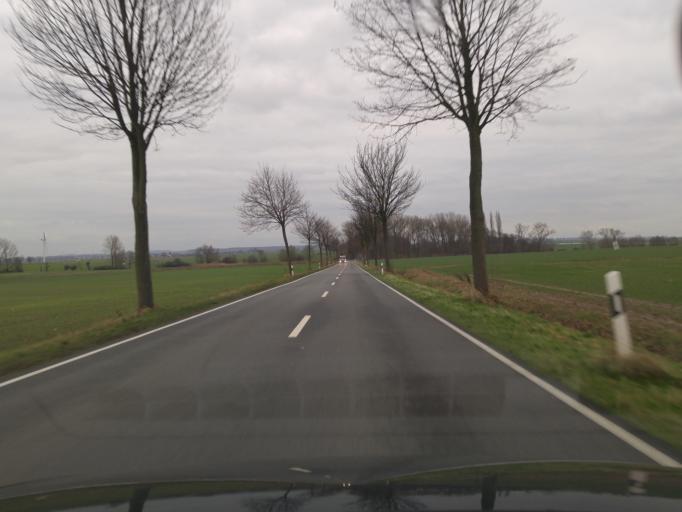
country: DE
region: Lower Saxony
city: Ilsede
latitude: 52.2362
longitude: 10.1710
